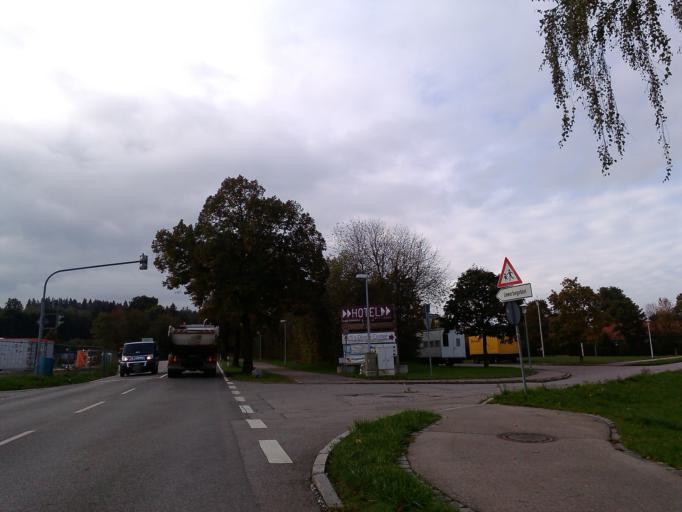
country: DE
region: Bavaria
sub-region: Upper Bavaria
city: Alling
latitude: 48.1352
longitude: 11.2987
